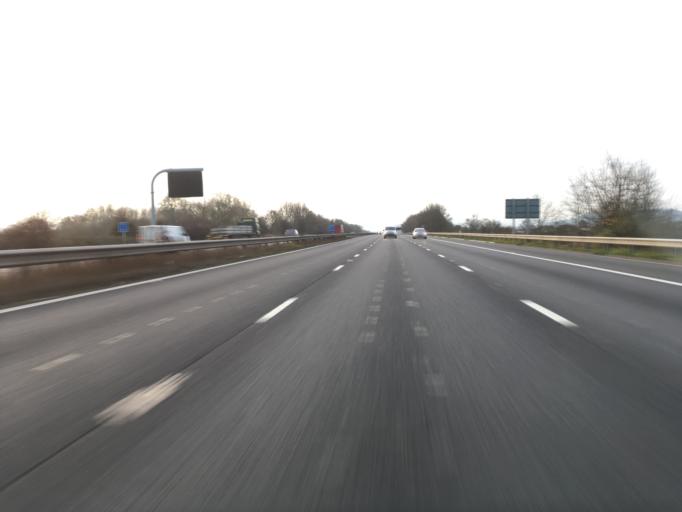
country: GB
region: England
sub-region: Gloucestershire
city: Uckington
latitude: 51.9053
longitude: -2.1519
